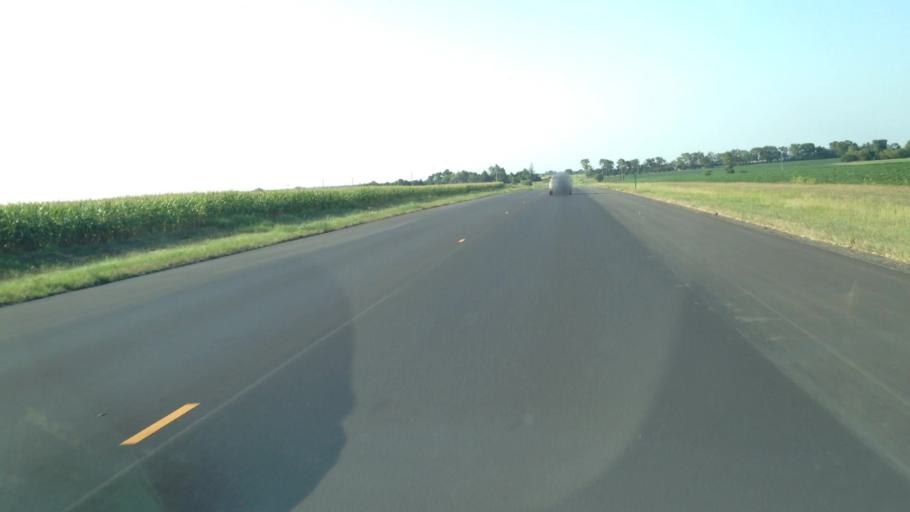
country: US
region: Kansas
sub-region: Anderson County
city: Garnett
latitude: 38.4440
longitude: -95.2487
